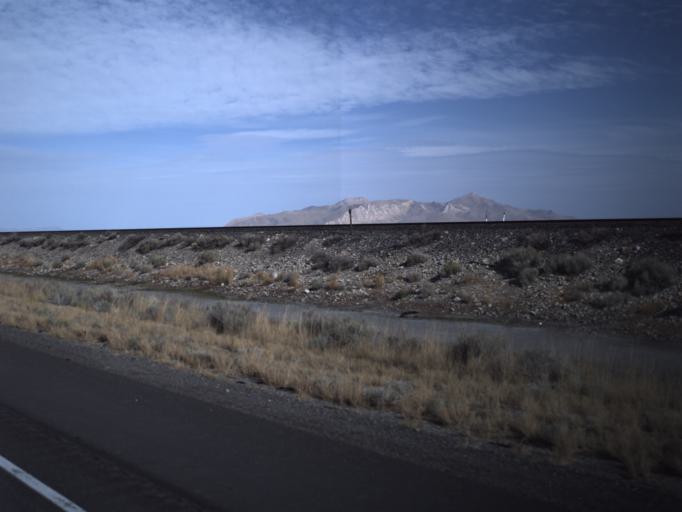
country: US
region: Utah
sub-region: Tooele County
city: Grantsville
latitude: 40.6759
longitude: -112.4019
